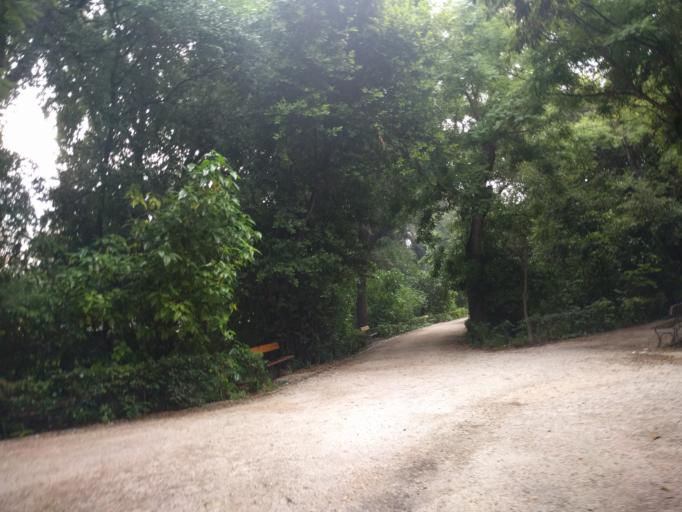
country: GR
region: Attica
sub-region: Nomarchia Athinas
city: Vyronas
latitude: 37.9732
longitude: 23.7398
